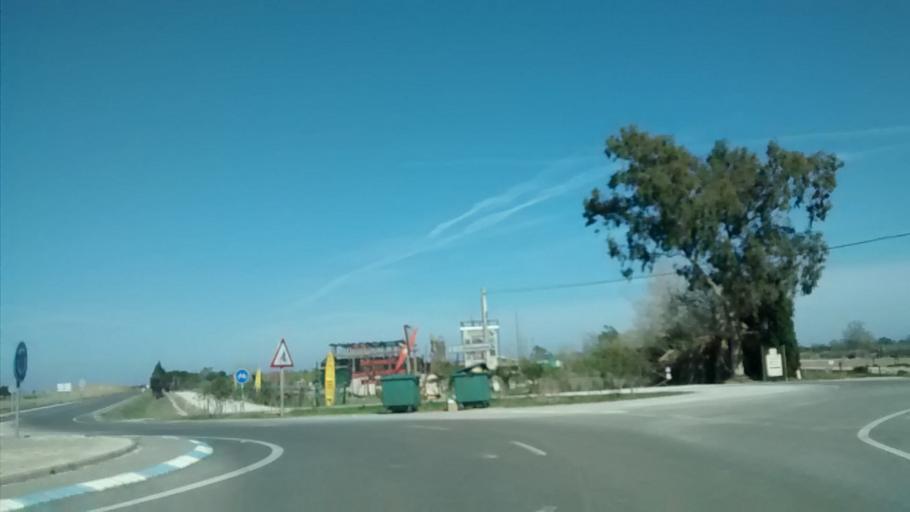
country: ES
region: Catalonia
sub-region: Provincia de Tarragona
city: Deltebre
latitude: 40.7075
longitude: 0.8119
